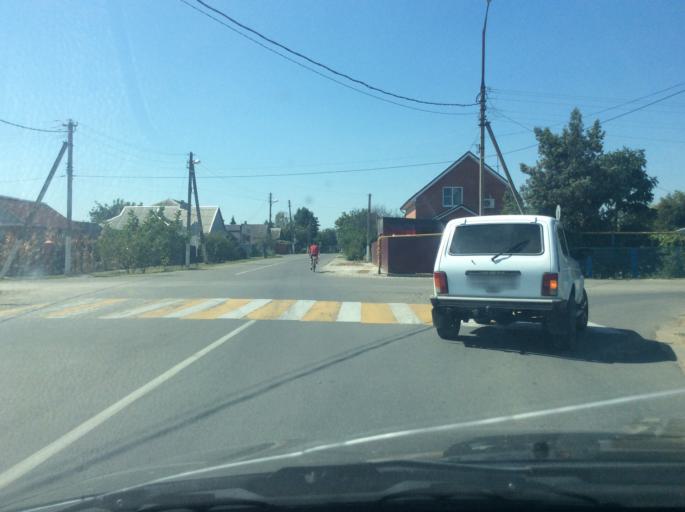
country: RU
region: Krasnodarskiy
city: Slavyansk-na-Kubani
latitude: 45.2502
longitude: 38.1075
